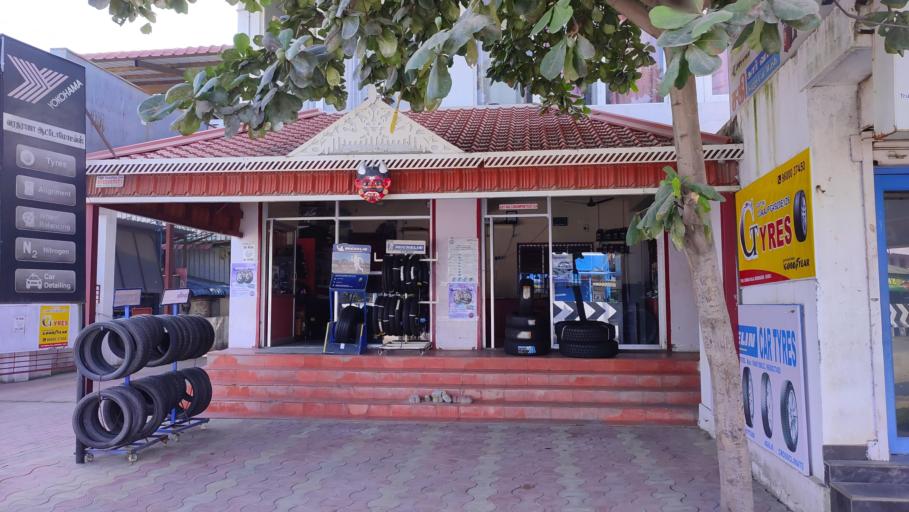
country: IN
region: Tamil Nadu
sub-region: Krishnagiri
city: Krishnagiri
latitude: 12.5227
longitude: 78.2295
